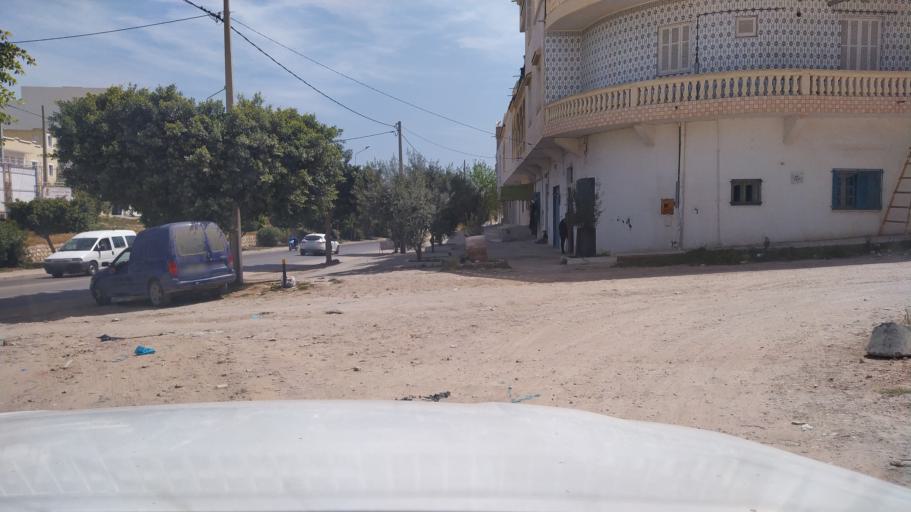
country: TN
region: Al Mahdiyah
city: Zouila
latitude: 35.5058
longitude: 11.0353
